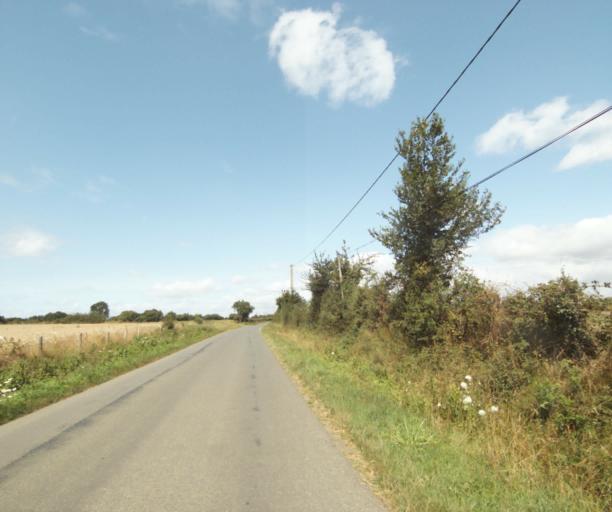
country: FR
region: Pays de la Loire
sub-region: Departement de la Sarthe
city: Sable-sur-Sarthe
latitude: 47.8417
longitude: -0.3674
